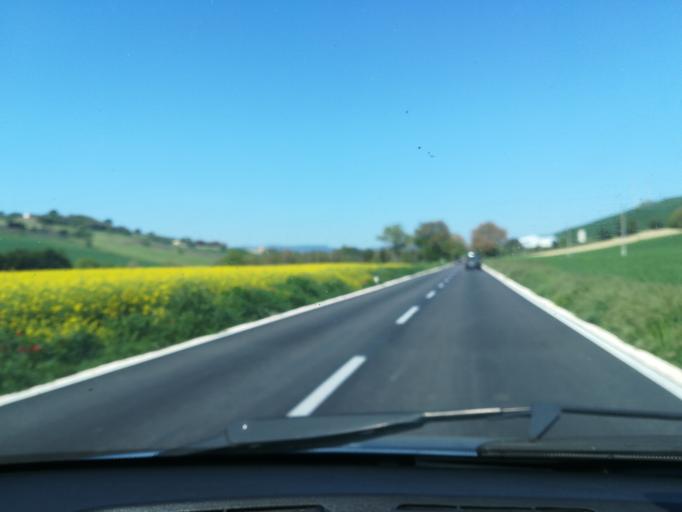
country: IT
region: The Marches
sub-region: Provincia di Macerata
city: Villa Potenza
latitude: 43.3274
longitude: 13.3977
